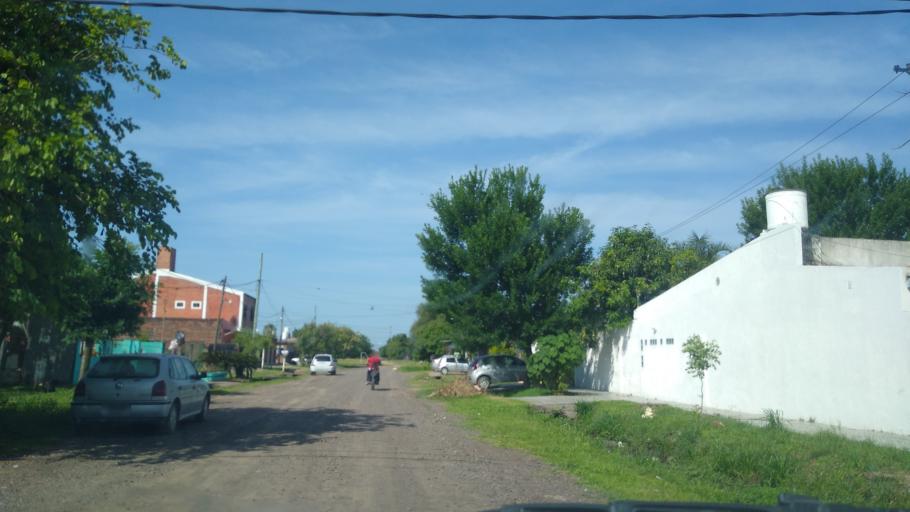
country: AR
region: Chaco
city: Barranqueras
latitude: -27.4918
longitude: -58.9513
